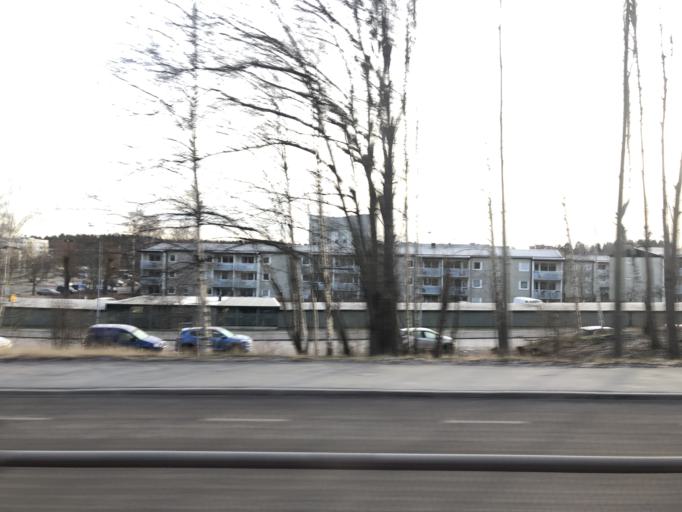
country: SE
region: Stockholm
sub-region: Jarfalla Kommun
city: Jakobsberg
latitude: 59.4125
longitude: 17.7968
